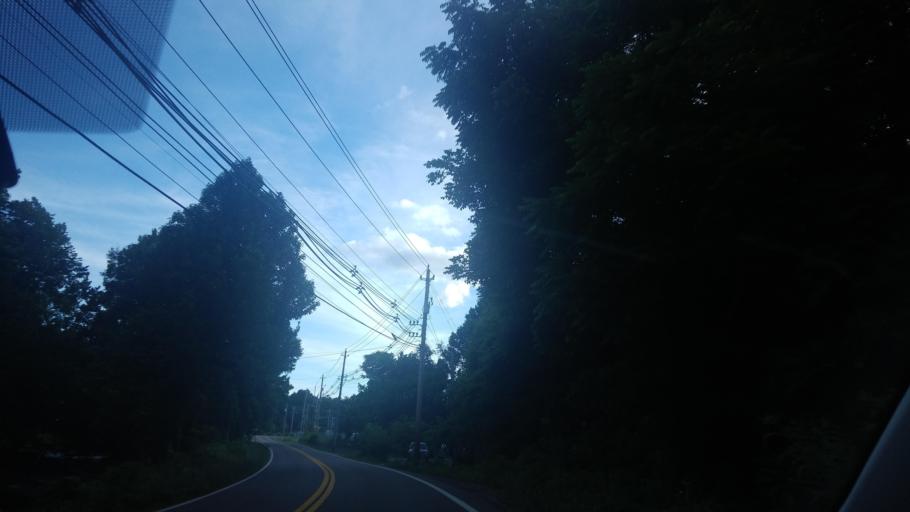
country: US
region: Tennessee
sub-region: Cocke County
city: Newport
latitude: 35.8066
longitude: -83.2486
